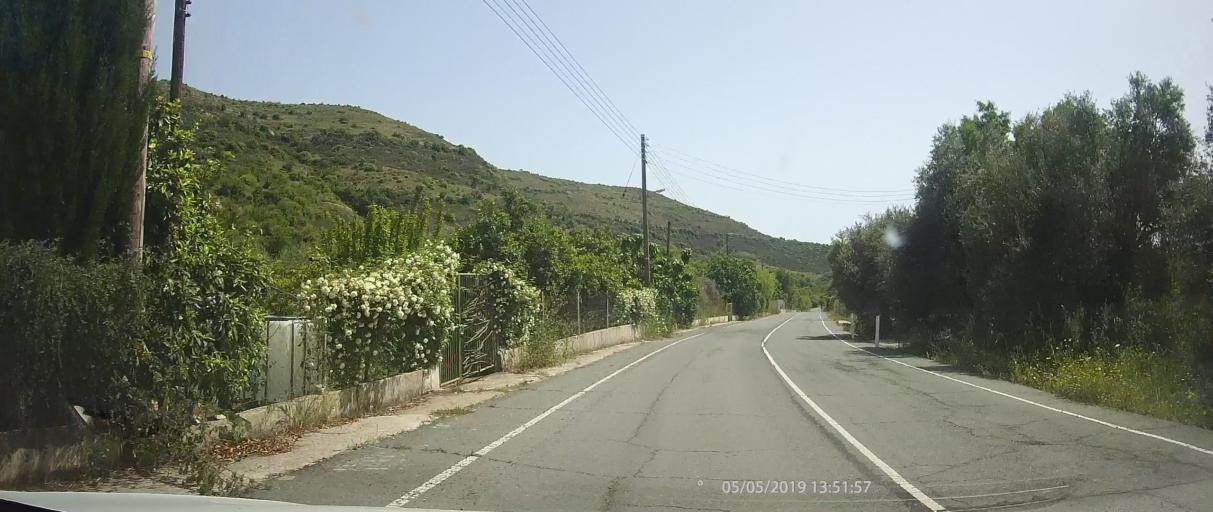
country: CY
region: Limassol
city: Pachna
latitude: 34.8340
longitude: 32.7364
